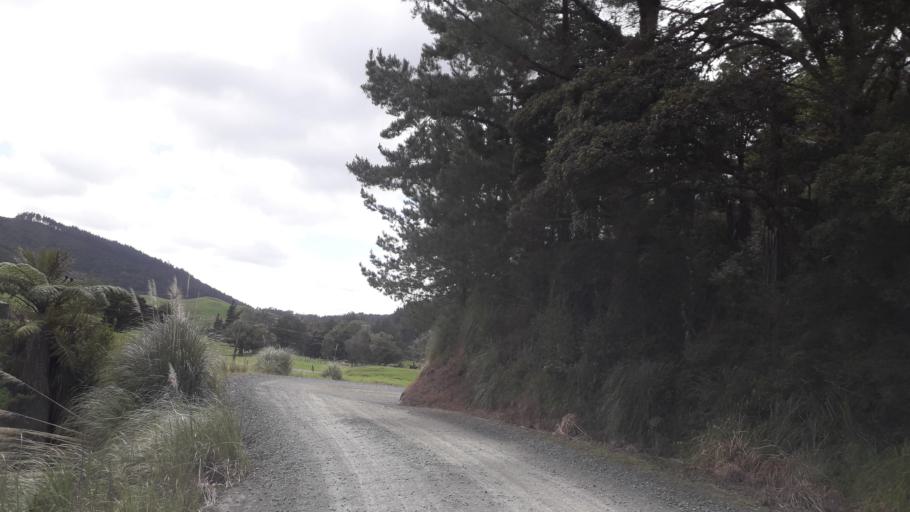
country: NZ
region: Northland
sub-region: Far North District
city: Kaitaia
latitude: -35.1879
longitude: 173.2935
